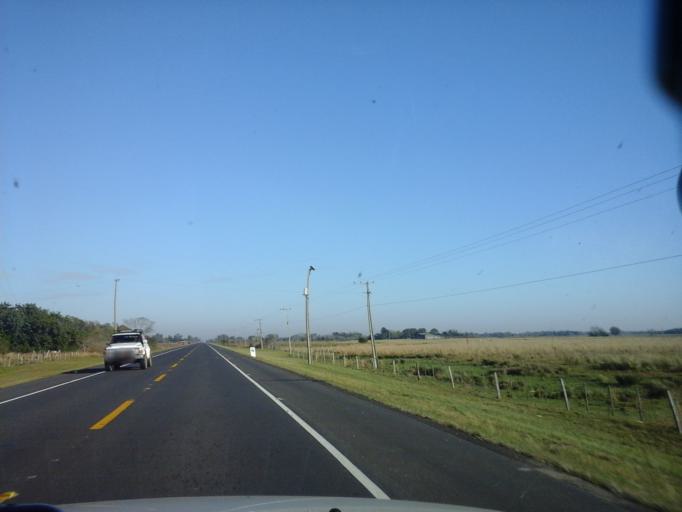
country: PY
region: Neembucu
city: Pilar
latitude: -26.8581
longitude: -58.0072
